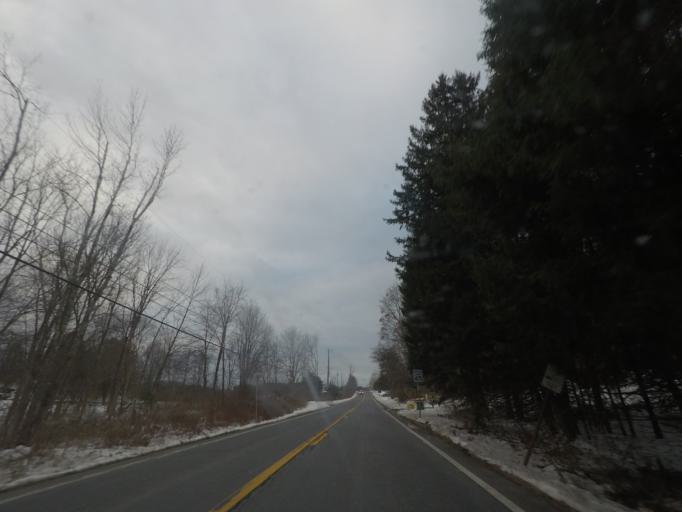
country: US
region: New York
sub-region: Ulster County
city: New Paltz
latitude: 41.7020
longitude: -74.0976
